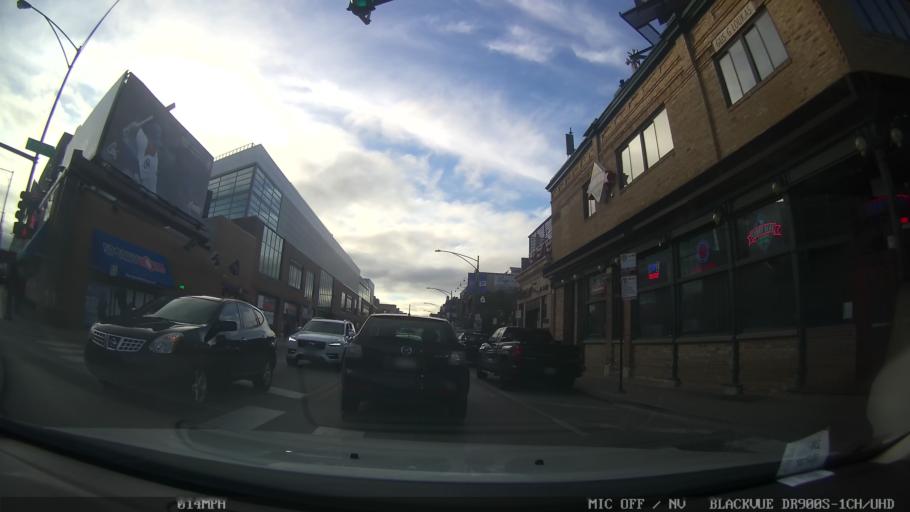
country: US
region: Illinois
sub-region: Cook County
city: Lincolnwood
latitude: 41.9471
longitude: -87.6565
